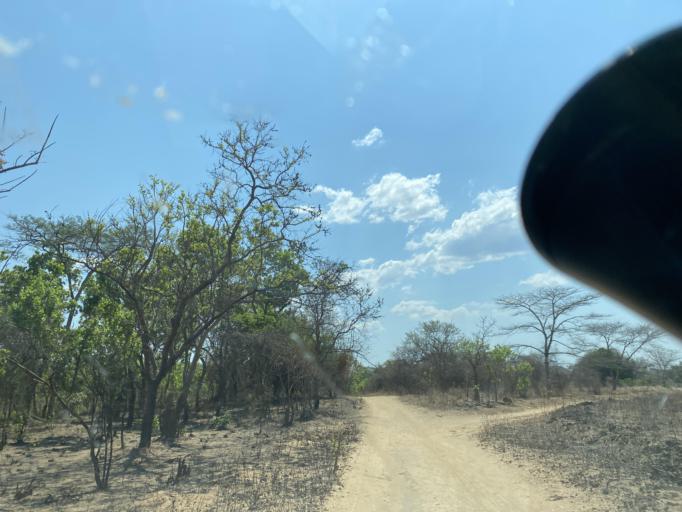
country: ZM
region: Lusaka
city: Chongwe
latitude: -15.0817
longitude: 29.5020
